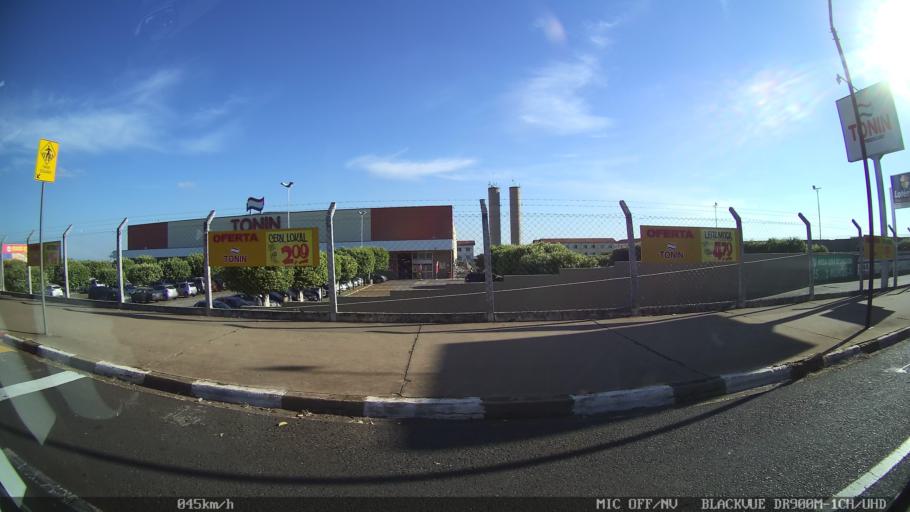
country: BR
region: Sao Paulo
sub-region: Franca
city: Franca
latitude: -20.5060
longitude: -47.4035
